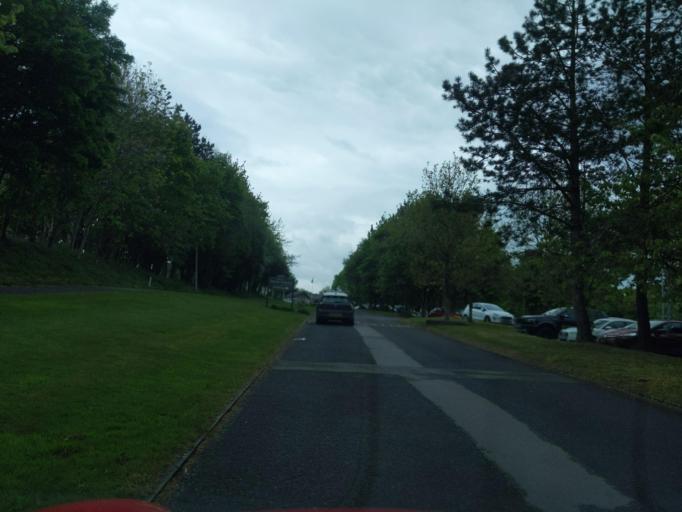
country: GB
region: England
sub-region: Cornwall
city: Saltash
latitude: 50.4211
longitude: -4.2141
